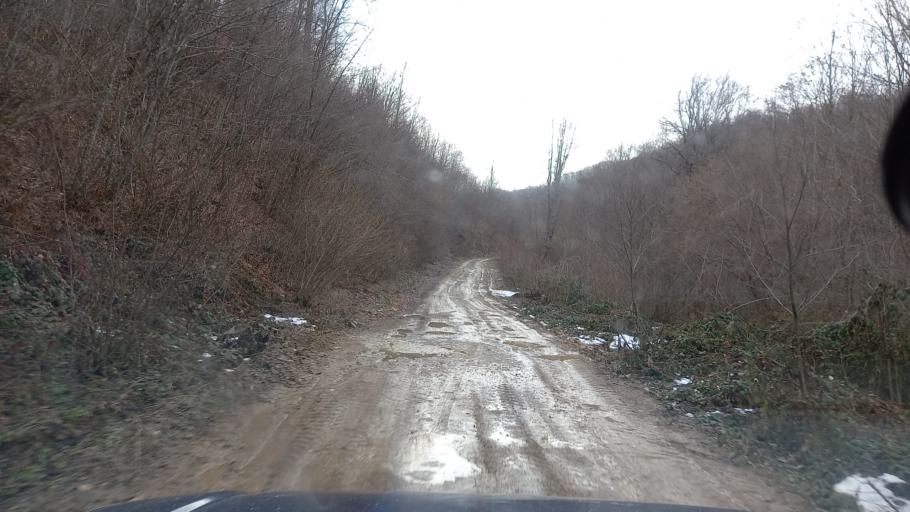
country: RU
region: Adygeya
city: Kamennomostskiy
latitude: 44.1732
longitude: 40.2999
